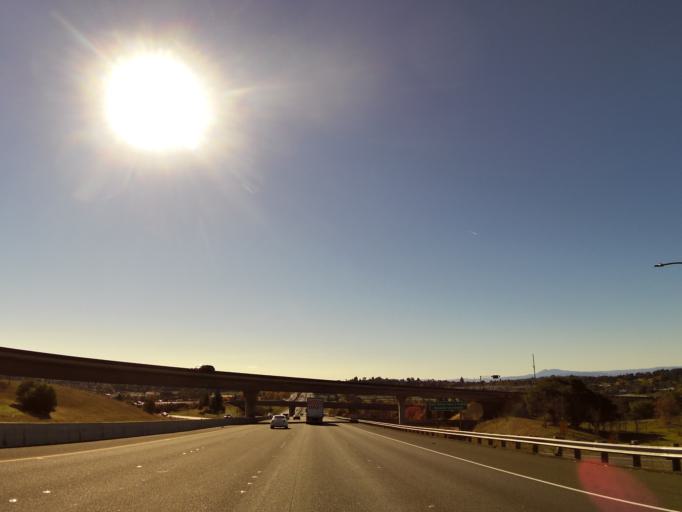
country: US
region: California
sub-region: Napa County
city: American Canyon
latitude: 38.1421
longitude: -122.2183
